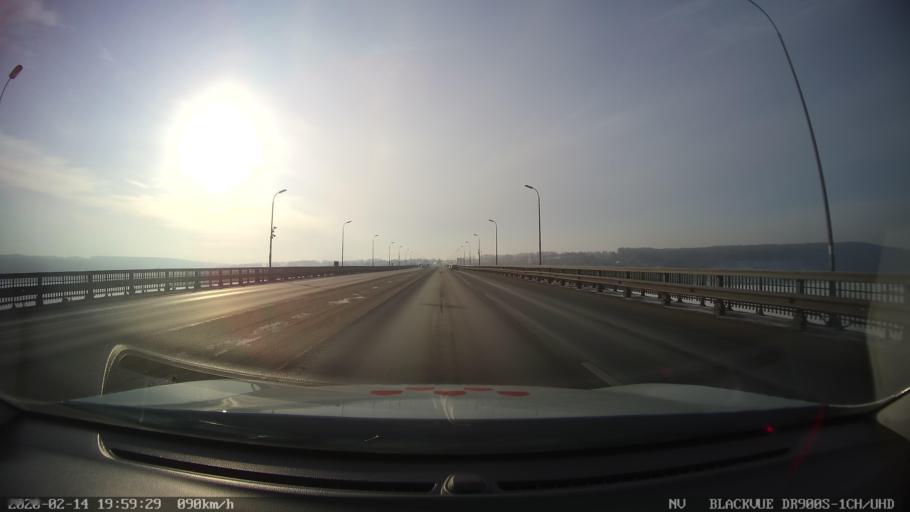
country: RU
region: Tatarstan
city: Osinovo
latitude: 55.7865
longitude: 48.8410
